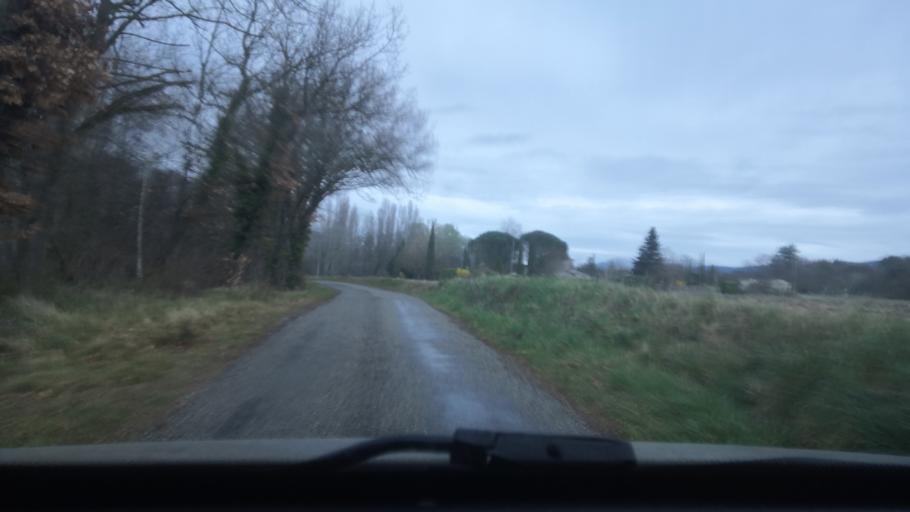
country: FR
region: Rhone-Alpes
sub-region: Departement de la Drome
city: Dieulefit
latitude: 44.5287
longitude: 5.0091
